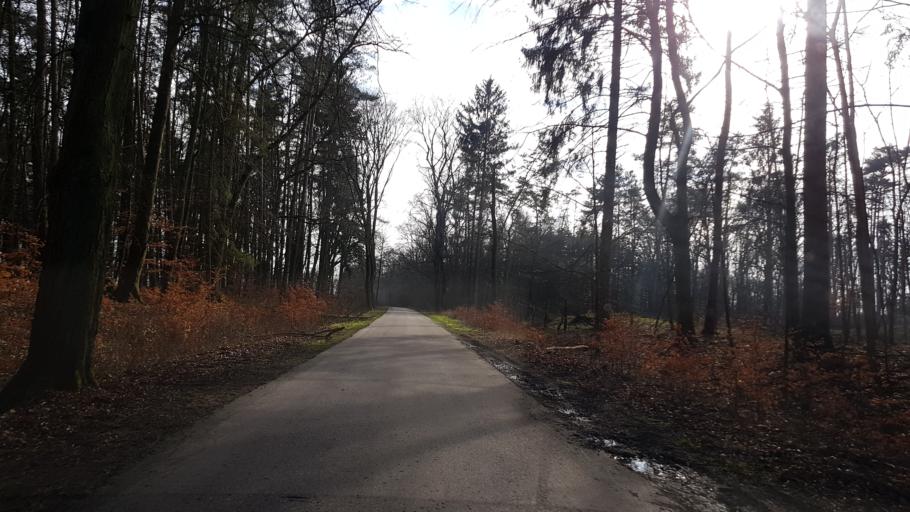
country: PL
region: West Pomeranian Voivodeship
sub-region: Powiat policki
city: Dobra
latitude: 53.5696
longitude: 14.3204
